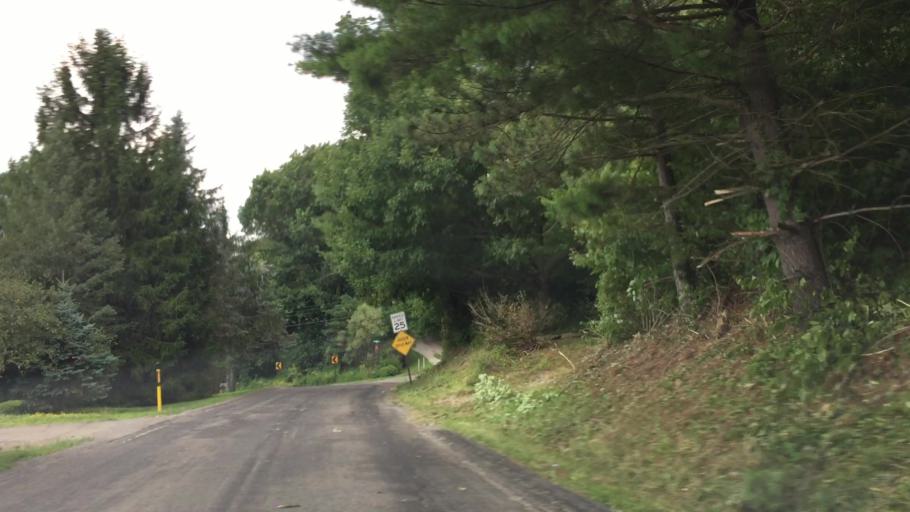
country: US
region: Pennsylvania
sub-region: Allegheny County
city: Enlow
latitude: 40.4508
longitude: -80.2287
